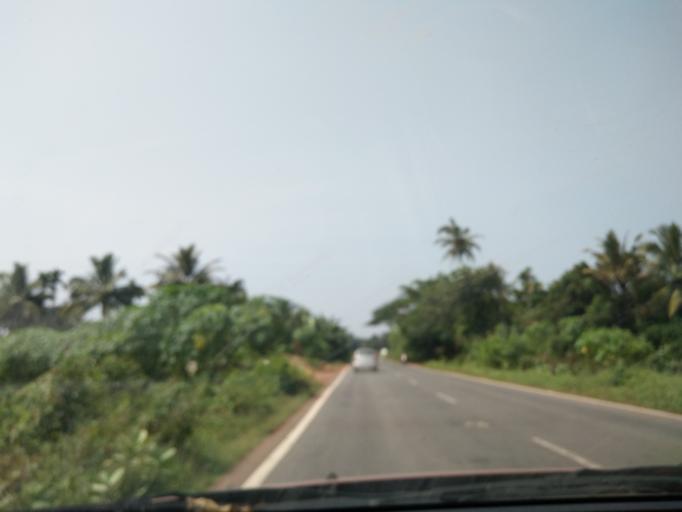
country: IN
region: Goa
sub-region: South Goa
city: Raia
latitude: 15.3031
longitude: 73.9547
